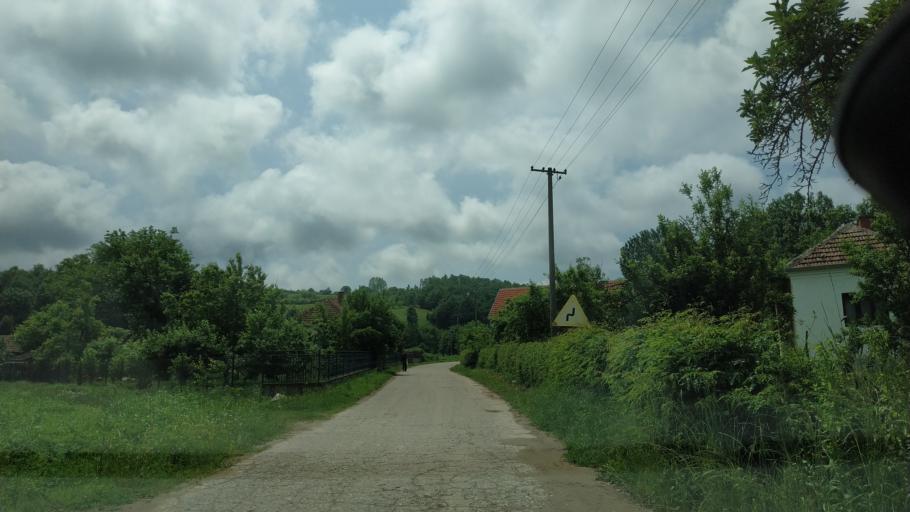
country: RS
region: Central Serbia
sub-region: Nisavski Okrug
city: Aleksinac
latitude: 43.4266
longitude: 21.7096
